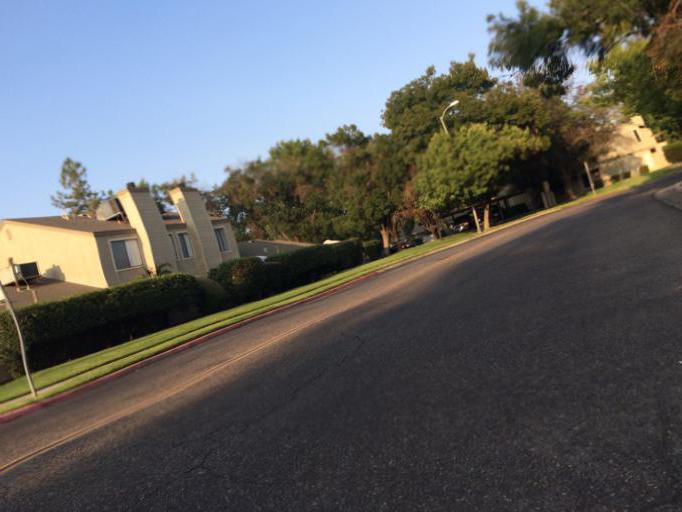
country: US
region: California
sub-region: Fresno County
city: Fresno
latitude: 36.8382
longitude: -119.8172
